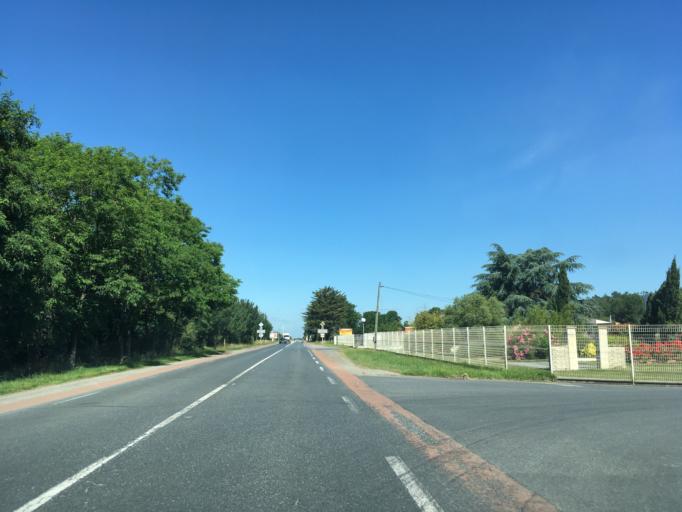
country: FR
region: Pays de la Loire
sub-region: Departement de la Vendee
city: Saint-Georges-de-Montaigu
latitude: 46.9411
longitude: -1.2837
